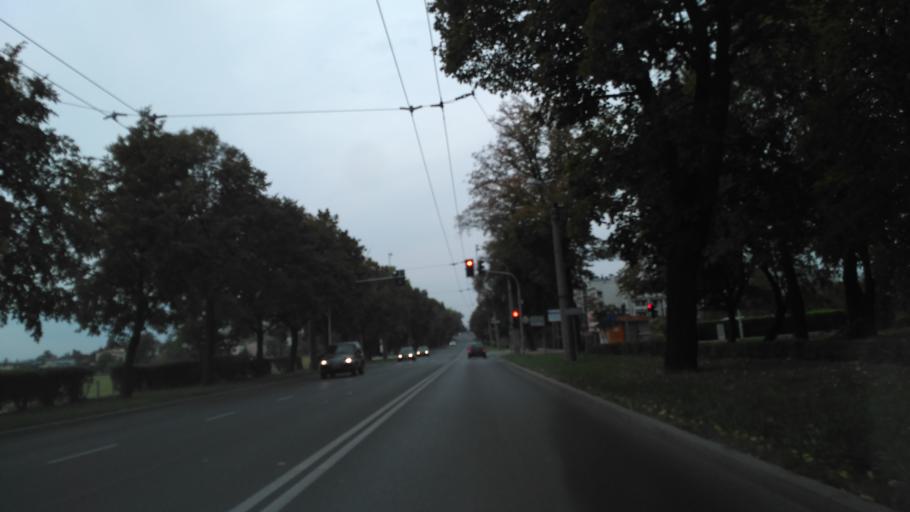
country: PL
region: Lublin Voivodeship
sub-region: Powiat lubelski
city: Lublin
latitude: 51.2268
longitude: 22.6040
